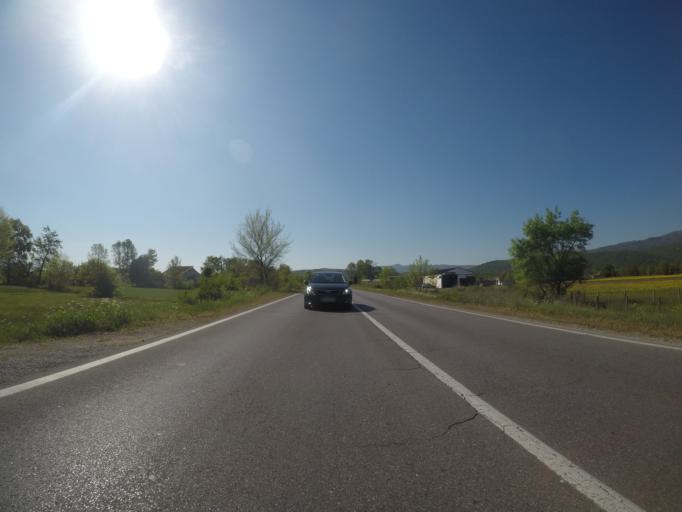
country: ME
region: Danilovgrad
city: Danilovgrad
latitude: 42.5282
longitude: 19.1173
